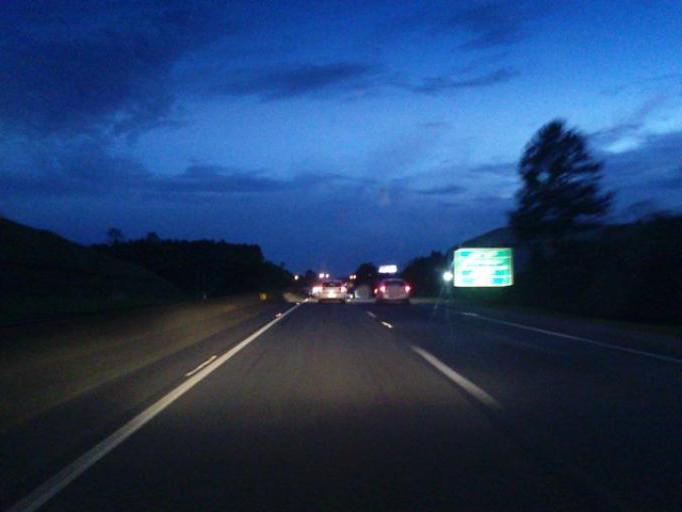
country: BR
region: Santa Catarina
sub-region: Barra Velha
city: Barra Velha
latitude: -26.6057
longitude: -48.7244
